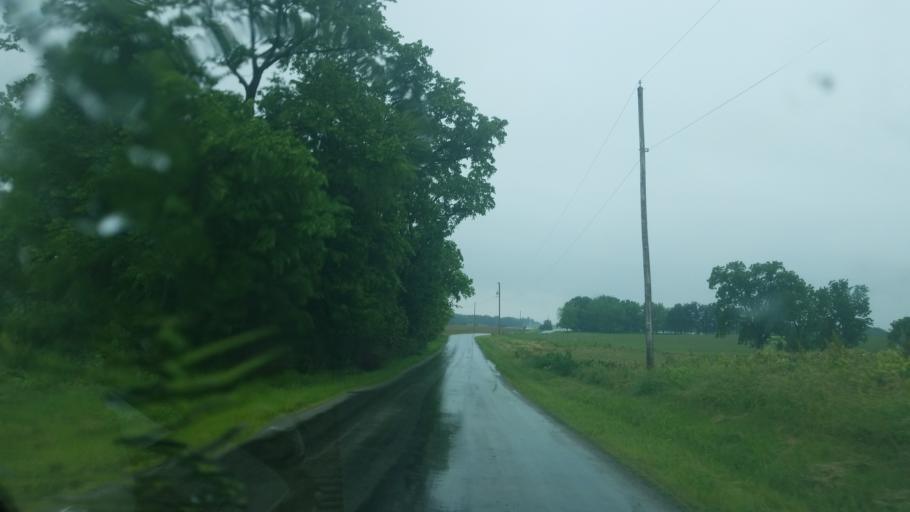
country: US
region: Ohio
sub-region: Huron County
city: Plymouth
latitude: 40.9915
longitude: -82.6019
